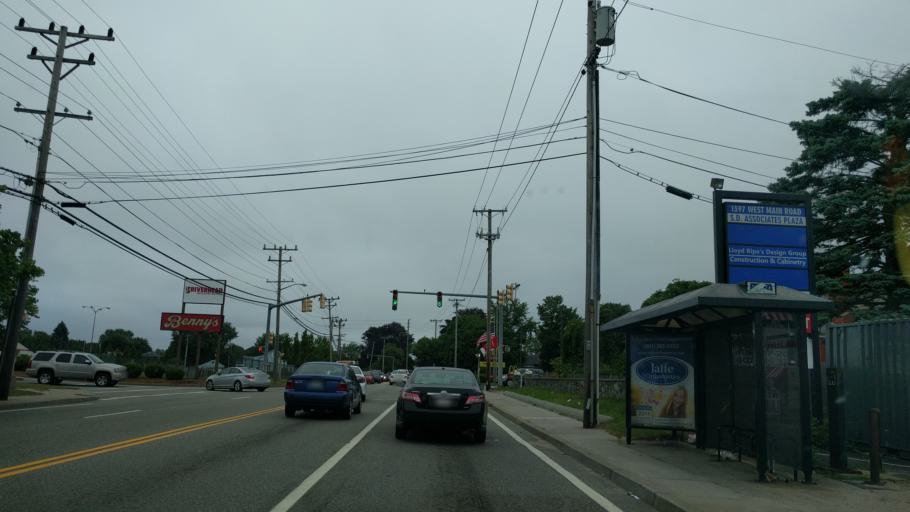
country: US
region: Rhode Island
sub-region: Newport County
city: Middletown
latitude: 41.5373
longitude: -71.2918
